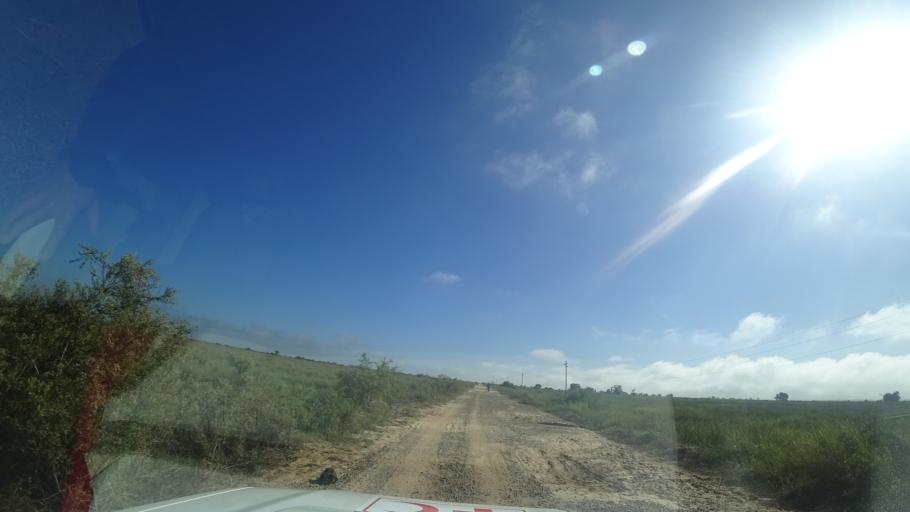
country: MZ
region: Sofala
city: Dondo
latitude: -19.4589
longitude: 34.5631
